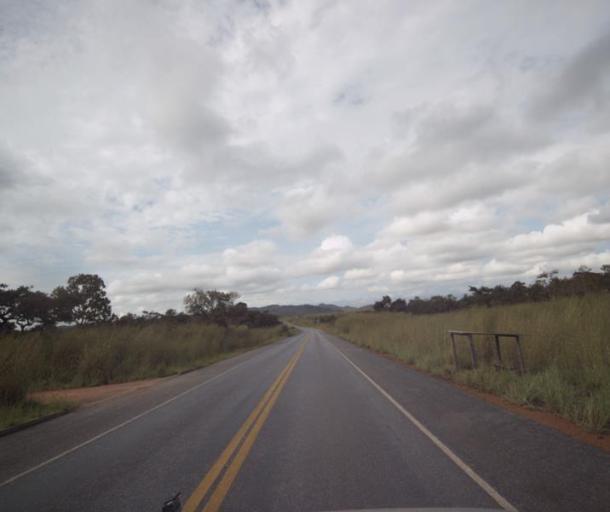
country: BR
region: Goias
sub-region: Pirenopolis
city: Pirenopolis
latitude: -15.5533
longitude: -48.6230
